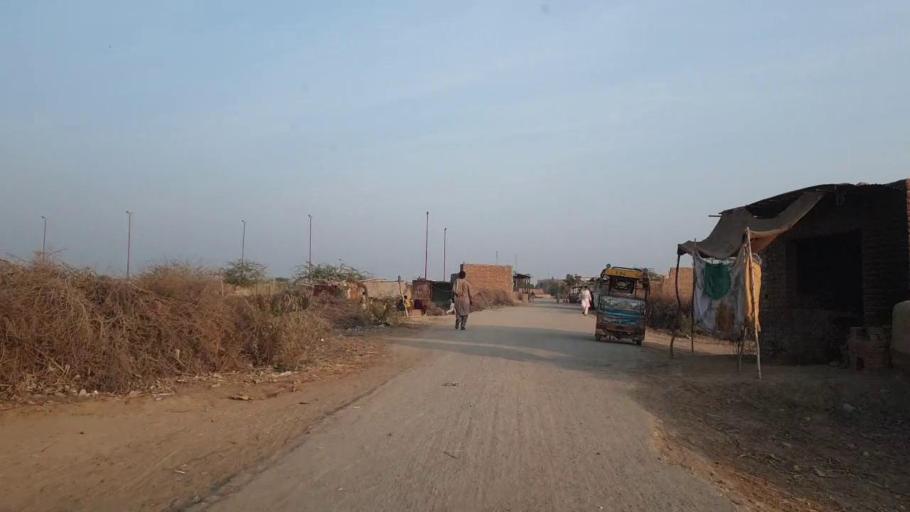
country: PK
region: Sindh
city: Matiari
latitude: 25.6068
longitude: 68.4332
